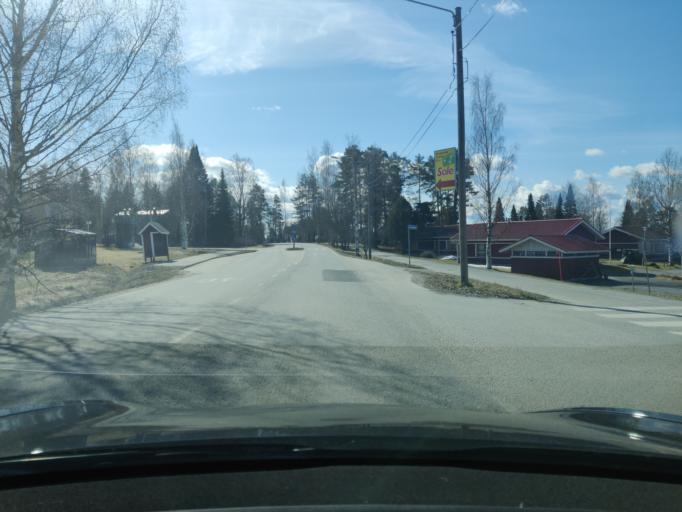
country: FI
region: Northern Savo
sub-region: Kuopio
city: Vehmersalmi
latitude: 62.7647
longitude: 28.0212
